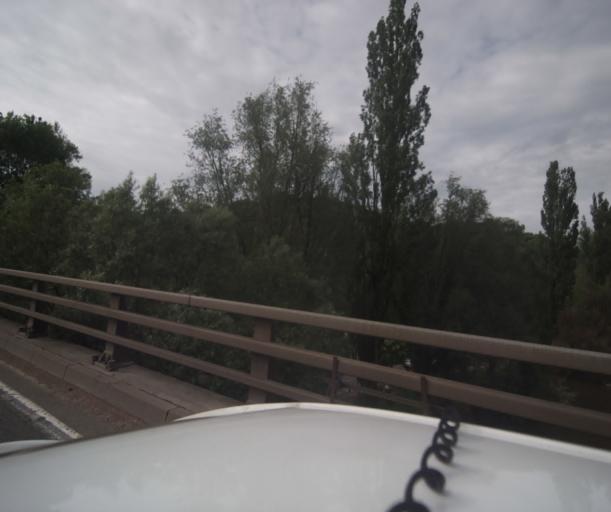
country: FR
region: Franche-Comte
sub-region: Departement du Doubs
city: Beure
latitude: 47.2114
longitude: 5.9971
